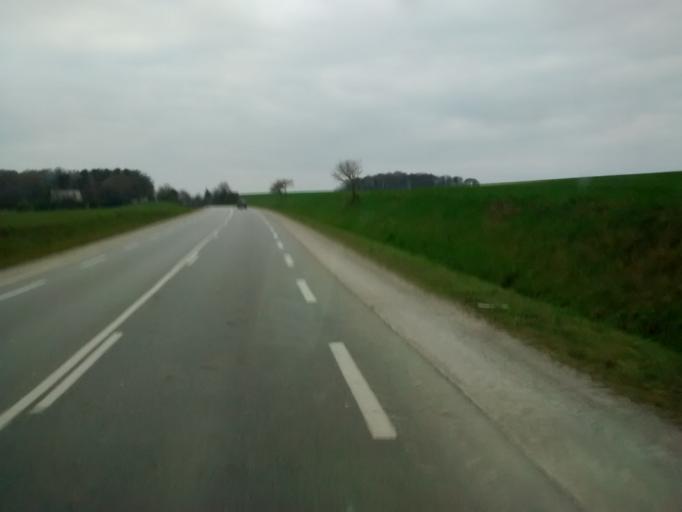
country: FR
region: Brittany
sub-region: Departement du Morbihan
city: Loyat
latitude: 47.9637
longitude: -2.3850
